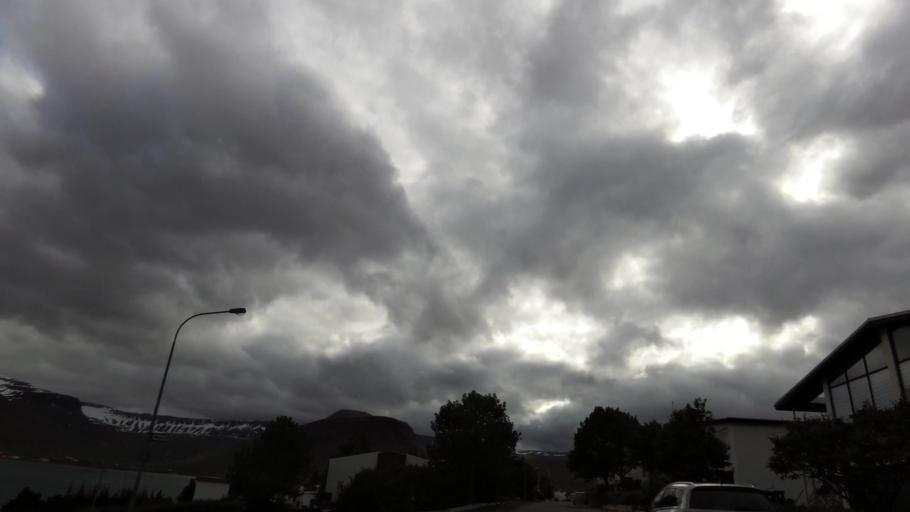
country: IS
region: Westfjords
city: Isafjoerdur
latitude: 66.0720
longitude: -23.1399
